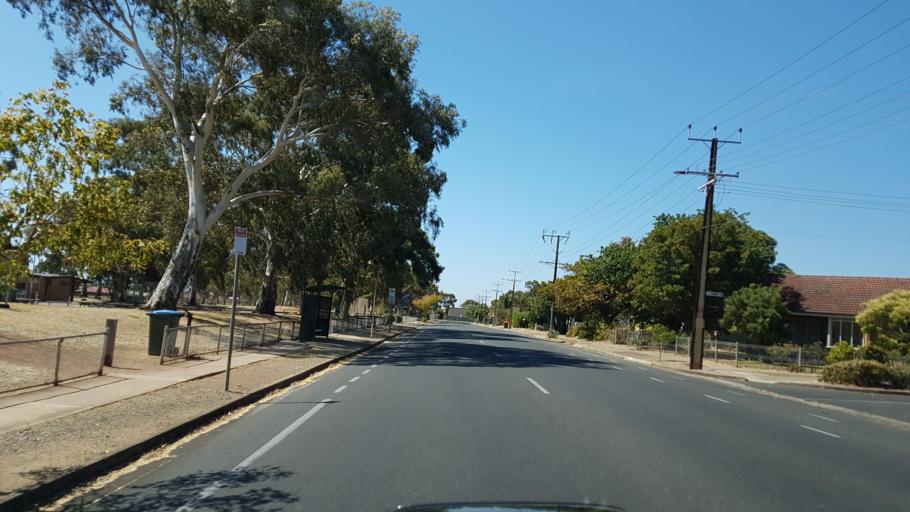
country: AU
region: South Australia
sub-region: Marion
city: Clovelly Park
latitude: -35.0031
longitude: 138.5655
